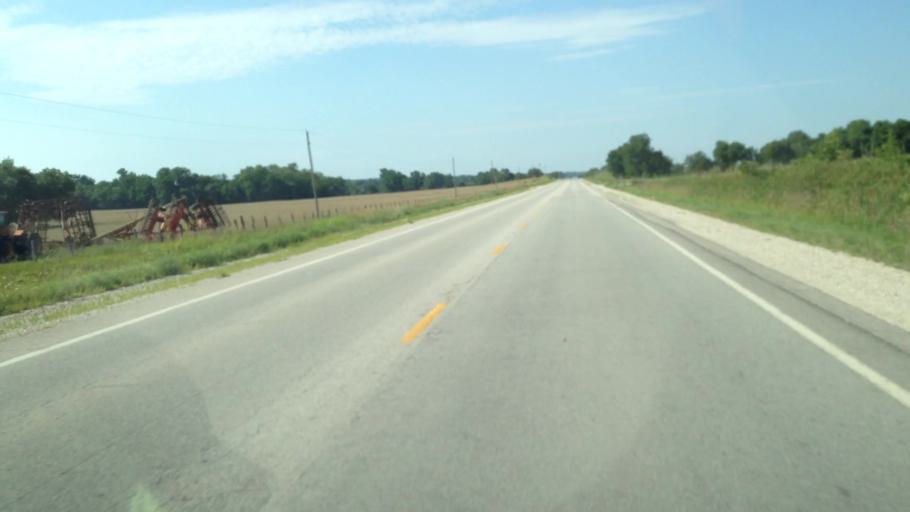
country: US
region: Kansas
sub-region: Neosho County
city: Erie
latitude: 37.4936
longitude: -95.2694
